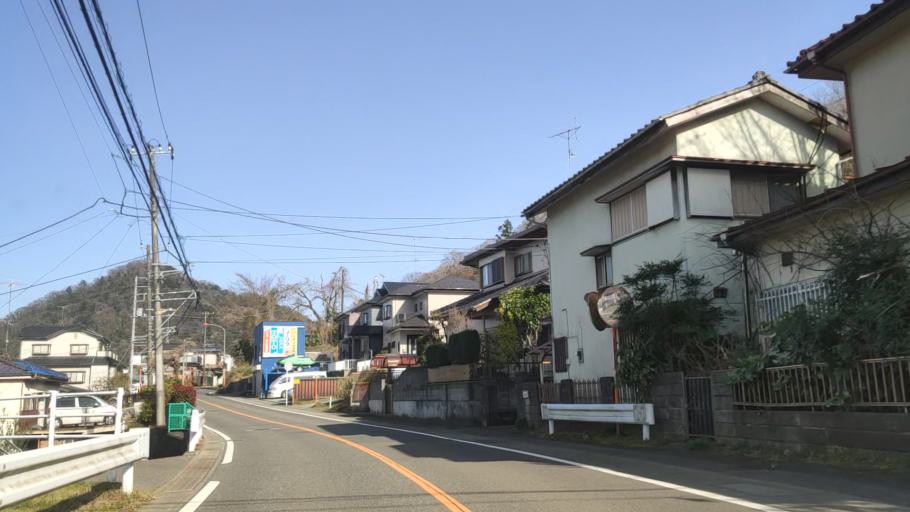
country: JP
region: Tokyo
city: Hachioji
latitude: 35.5824
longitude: 139.2651
